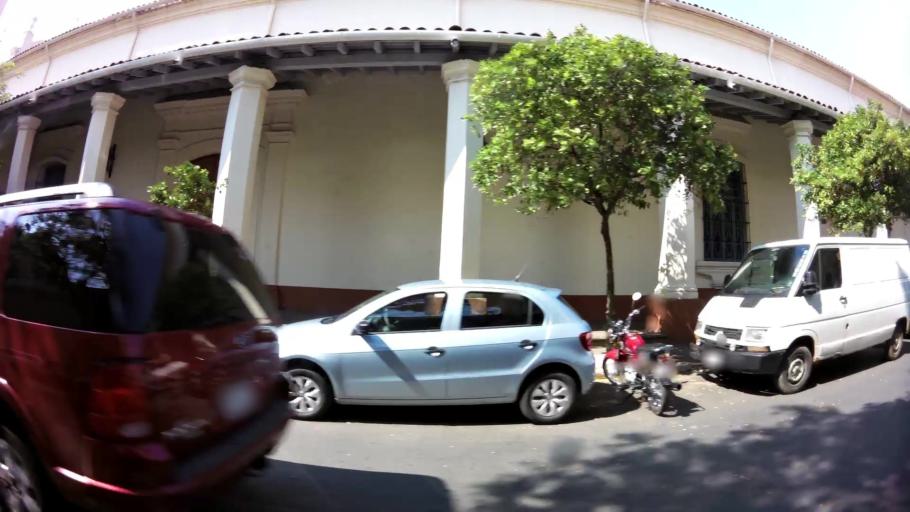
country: PY
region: Asuncion
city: Asuncion
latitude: -25.2818
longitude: -57.6325
